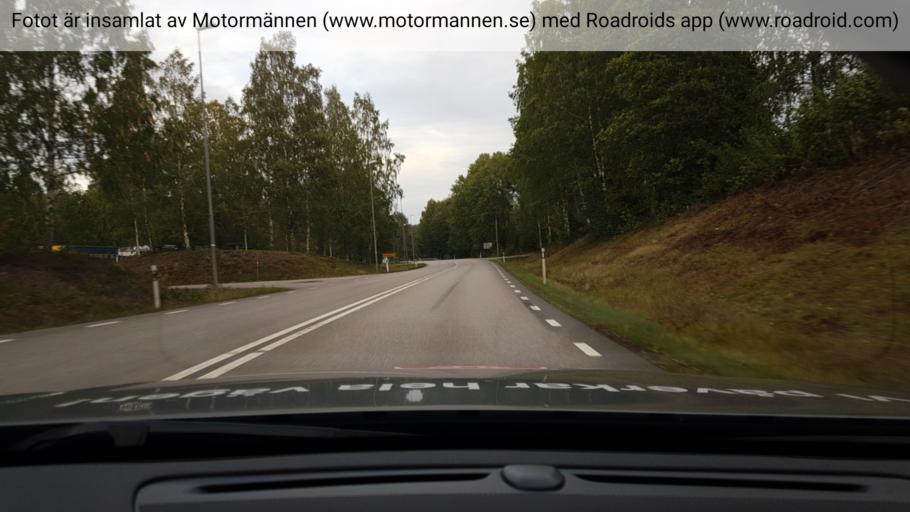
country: SE
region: Vaestra Goetaland
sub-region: Bengtsfors Kommun
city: Dals Langed
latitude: 59.0578
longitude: 12.4475
